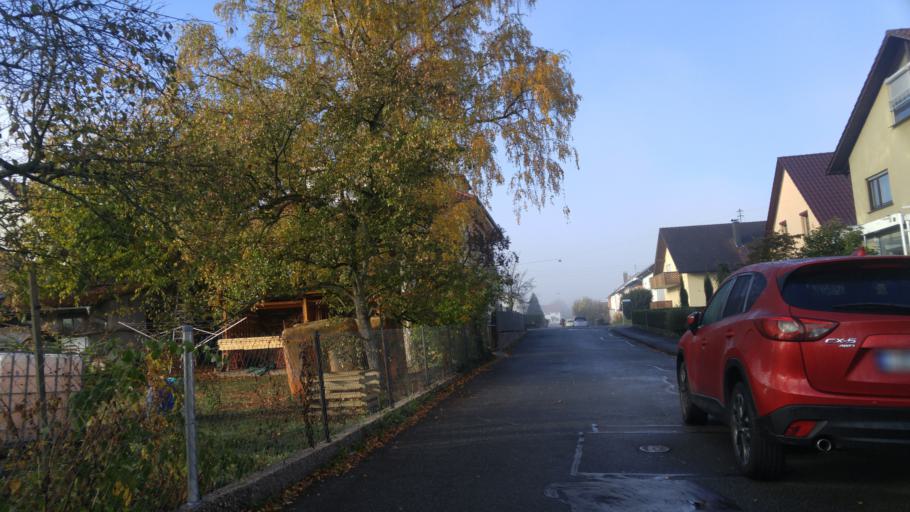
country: DE
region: Baden-Wuerttemberg
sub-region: Karlsruhe Region
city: Hassmersheim
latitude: 49.3027
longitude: 9.1466
